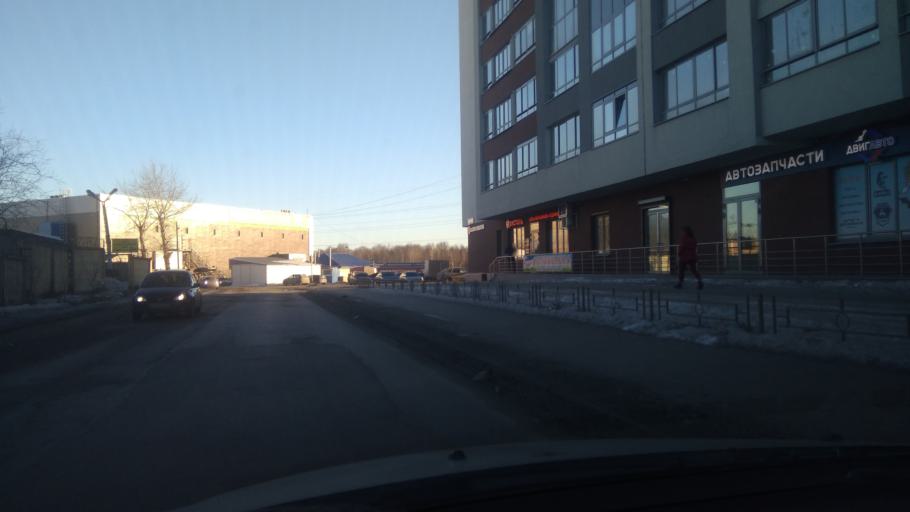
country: RU
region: Sverdlovsk
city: Istok
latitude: 56.8253
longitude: 60.6982
